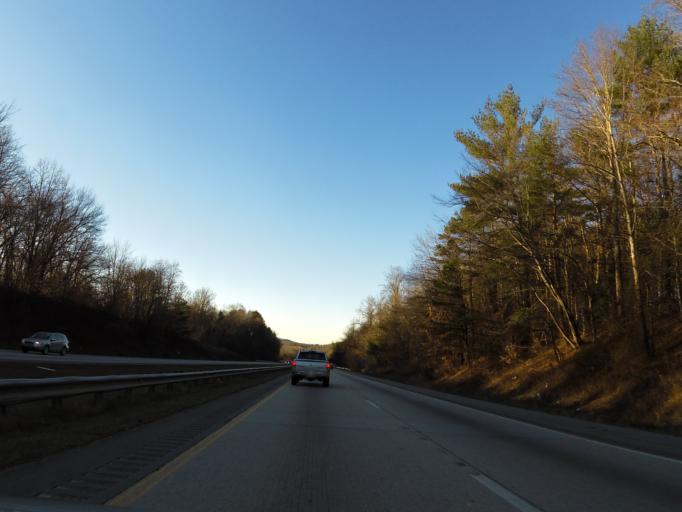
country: US
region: North Carolina
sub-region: Henderson County
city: Balfour
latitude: 35.3627
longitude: -82.4619
